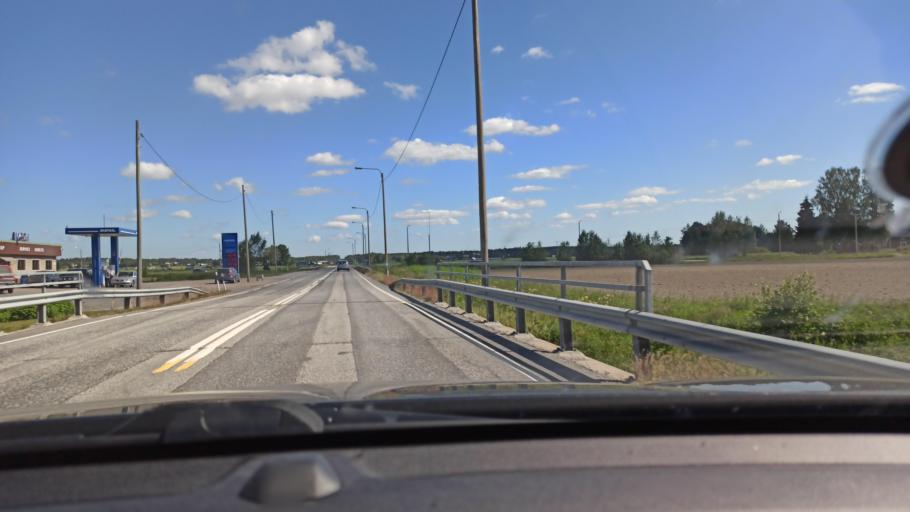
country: FI
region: Ostrobothnia
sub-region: Vaasa
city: Teeriniemi
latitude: 63.0005
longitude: 21.6707
